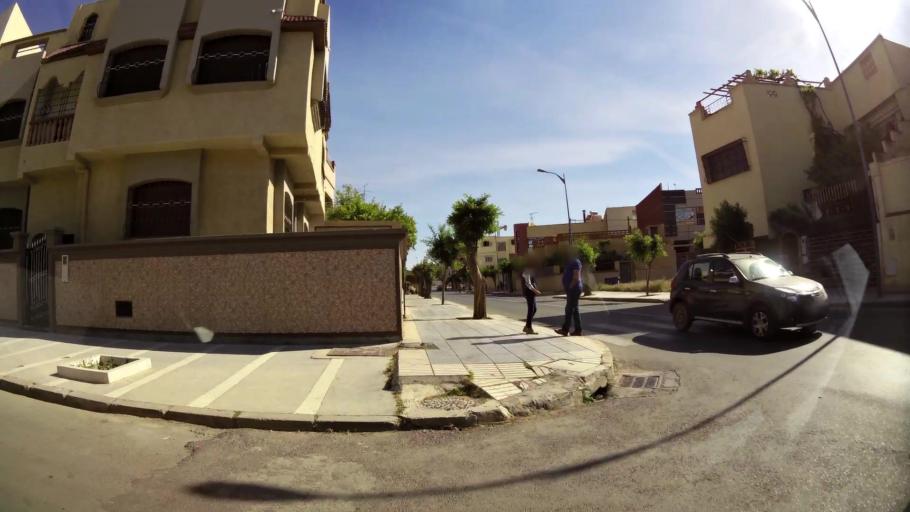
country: MA
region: Oriental
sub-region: Oujda-Angad
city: Oujda
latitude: 34.6667
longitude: -1.9130
